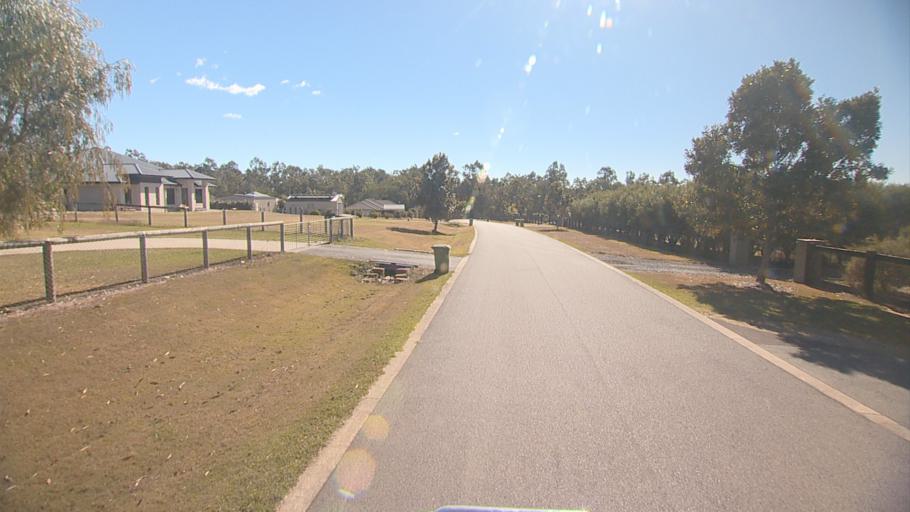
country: AU
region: Queensland
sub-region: Logan
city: North Maclean
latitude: -27.7573
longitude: 152.9643
